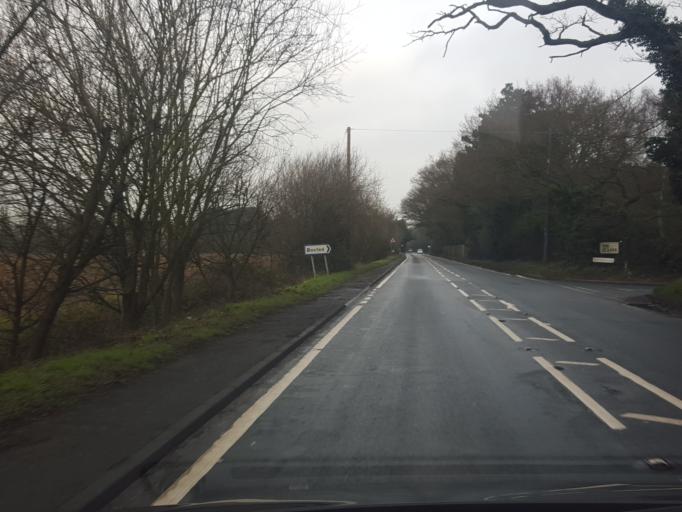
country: GB
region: England
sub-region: Essex
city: Great Horkesley
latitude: 51.9442
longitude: 0.8754
